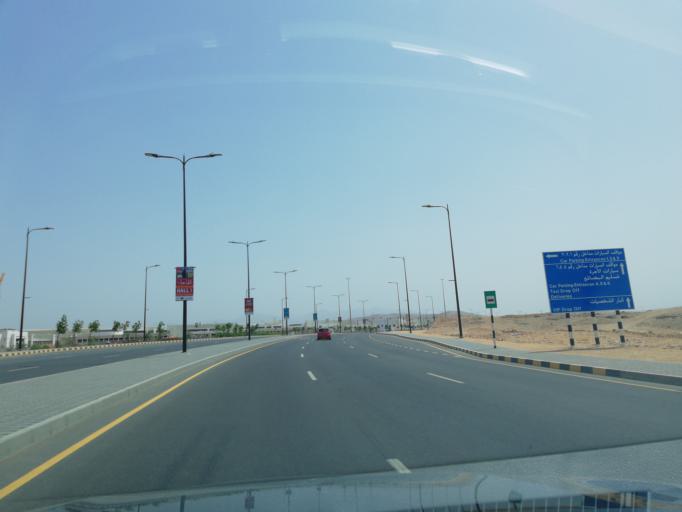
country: OM
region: Muhafazat Masqat
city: Bawshar
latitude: 23.5724
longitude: 58.3250
